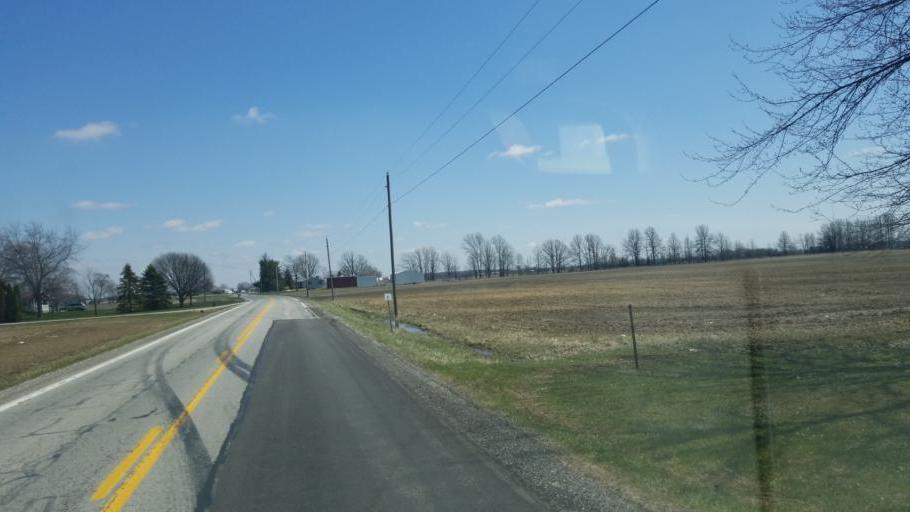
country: US
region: Ohio
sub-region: Marion County
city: Prospect
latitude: 40.4514
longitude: -83.1206
